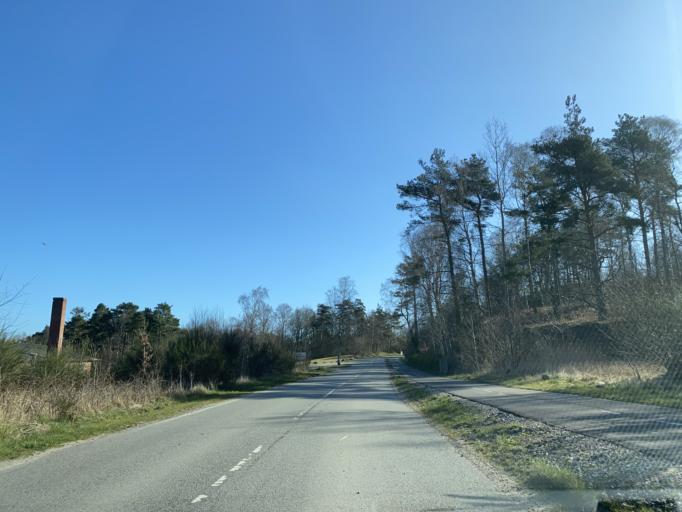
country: DK
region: Central Jutland
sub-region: Favrskov Kommune
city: Ulstrup
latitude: 56.3829
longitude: 9.7485
